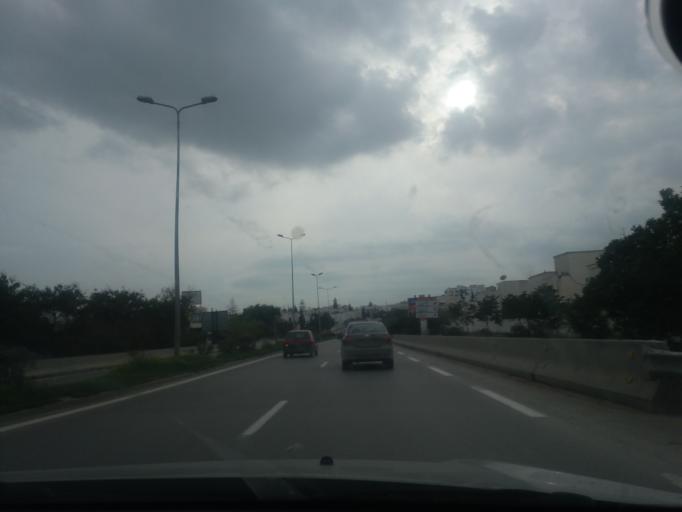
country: TN
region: Ariana
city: Ariana
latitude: 36.8617
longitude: 10.1726
